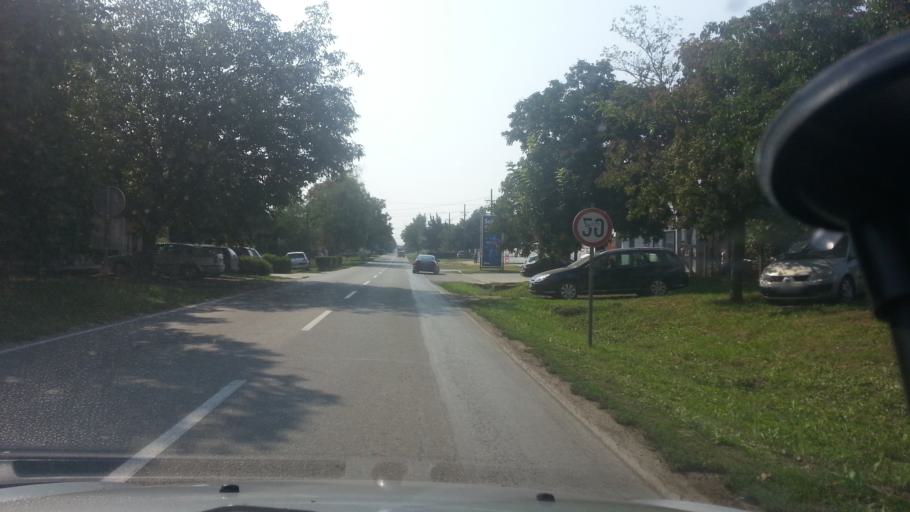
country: RS
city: Novi Banovci
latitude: 44.9650
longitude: 20.2814
